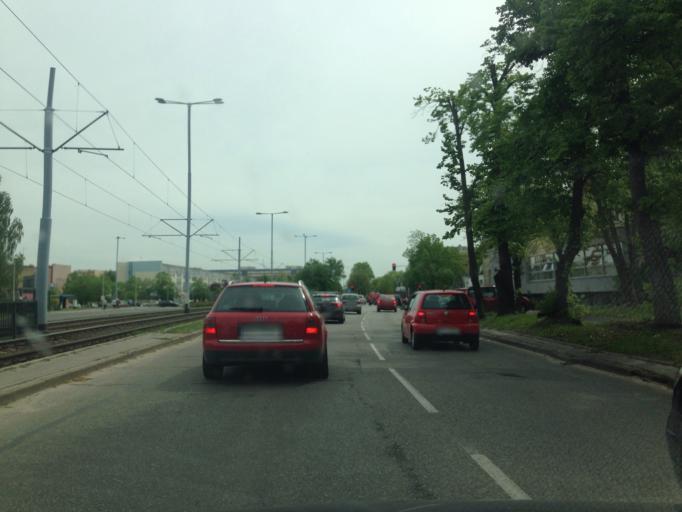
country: PL
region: Pomeranian Voivodeship
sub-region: Sopot
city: Sopot
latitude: 54.4174
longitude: 18.5861
